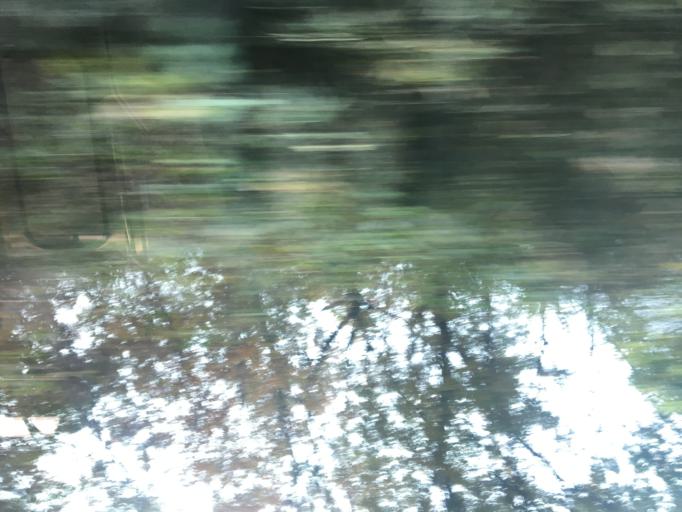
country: JP
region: Ibaraki
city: Iwase
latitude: 36.3433
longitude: 140.0689
